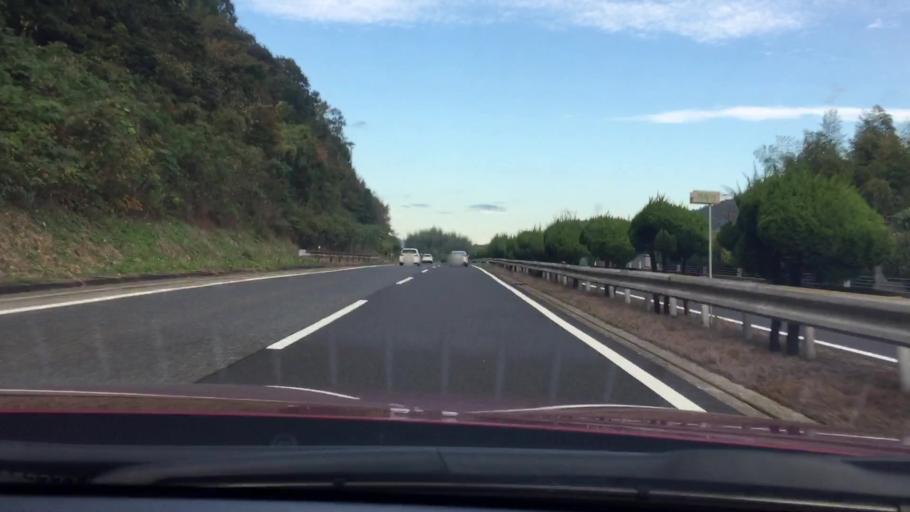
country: JP
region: Hyogo
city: Himeji
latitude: 34.9585
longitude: 134.7074
